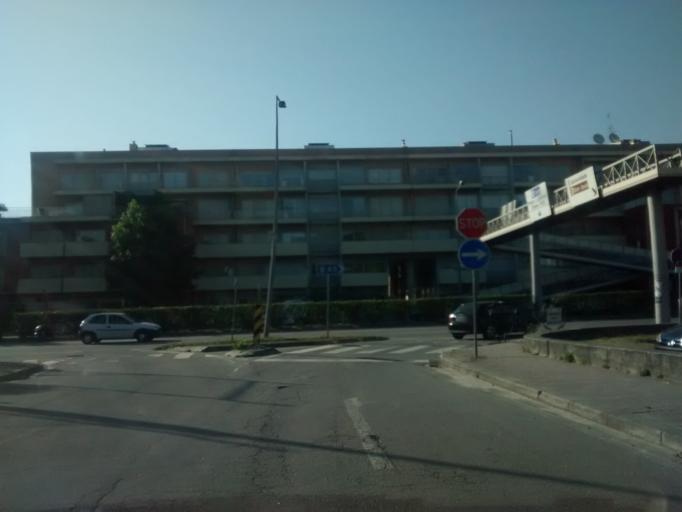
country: PT
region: Braga
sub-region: Braga
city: Braga
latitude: 41.5548
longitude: -8.4009
